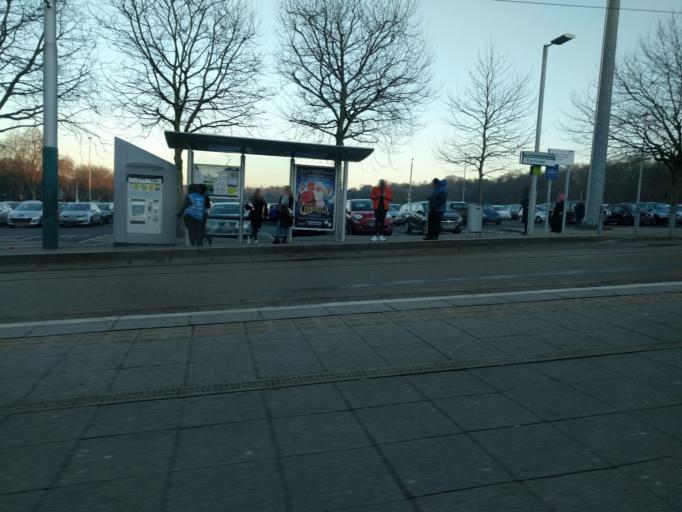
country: GB
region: England
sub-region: Nottingham
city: Nottingham
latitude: 52.9653
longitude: -1.1670
